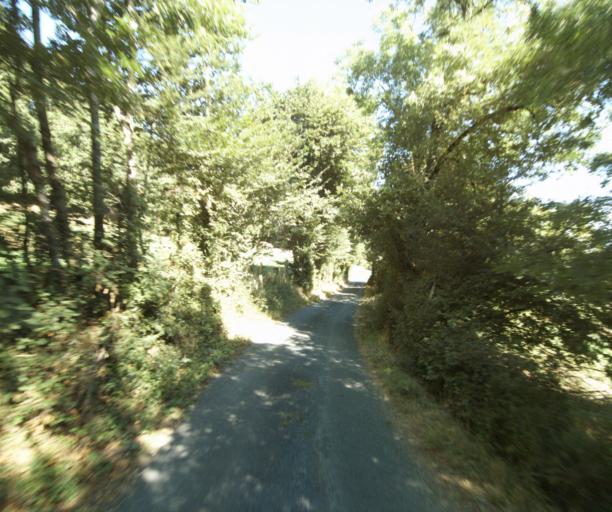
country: FR
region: Rhone-Alpes
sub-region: Departement du Rhone
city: Montrottier
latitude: 45.8067
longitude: 4.4957
